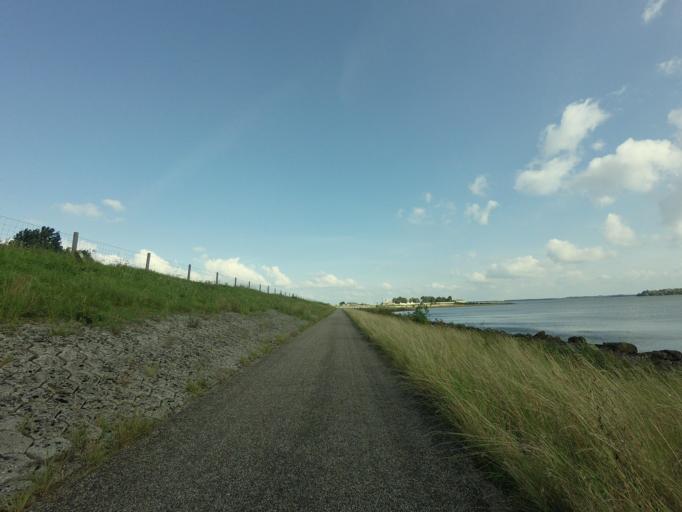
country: NL
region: Flevoland
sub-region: Gemeente Dronten
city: Dronten
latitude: 52.6130
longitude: 5.7381
